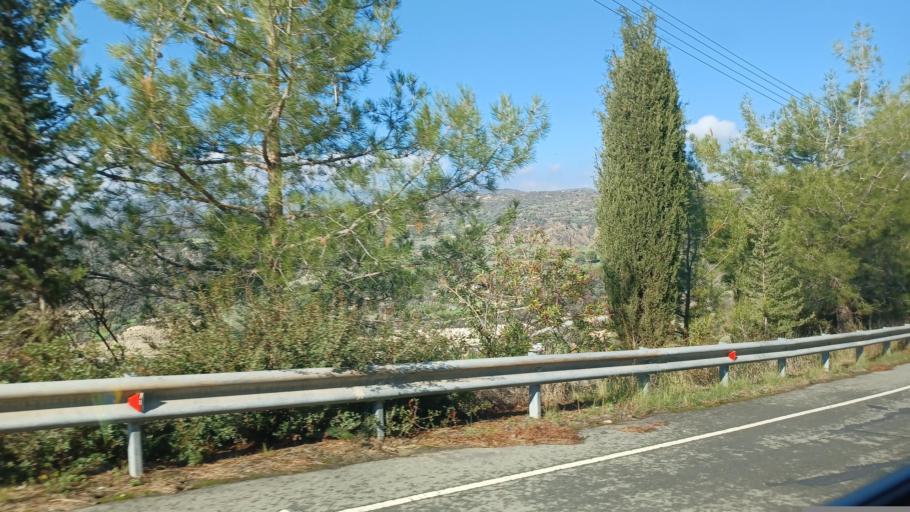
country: CY
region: Larnaka
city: Kofinou
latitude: 34.8434
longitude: 33.2970
